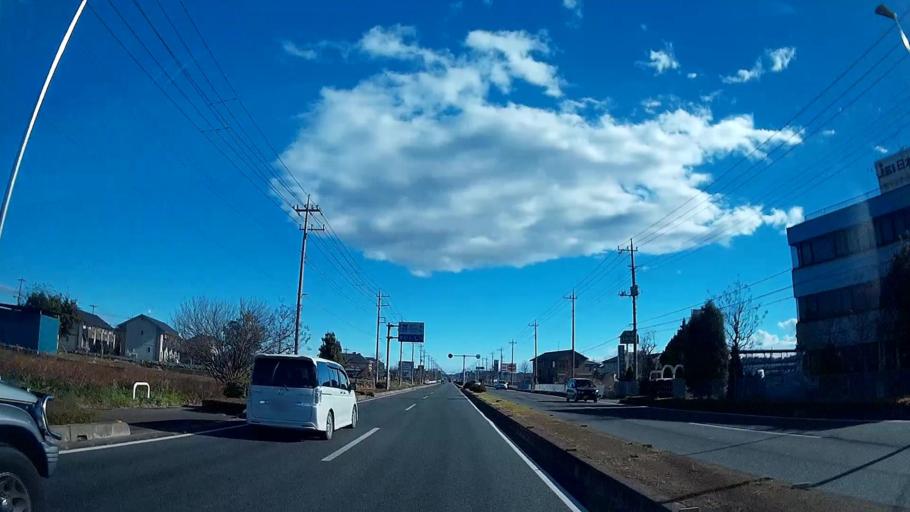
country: JP
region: Saitama
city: Yorii
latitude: 36.1218
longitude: 139.2188
